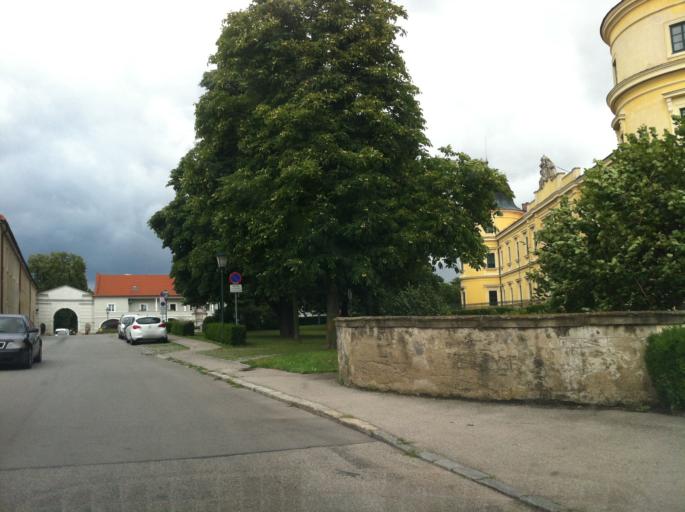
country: AT
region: Lower Austria
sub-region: Politischer Bezirk Tulln
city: Langenrohr
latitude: 48.2835
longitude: 16.0103
